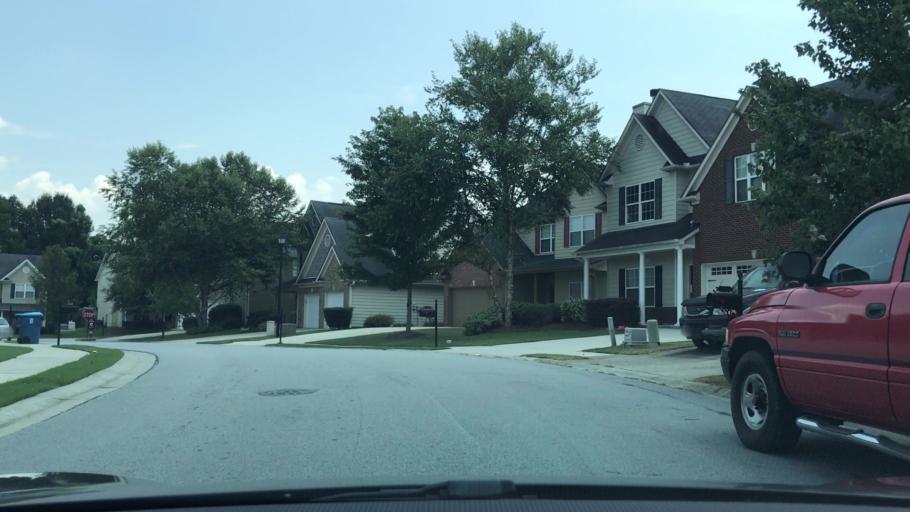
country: US
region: Georgia
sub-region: Jackson County
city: Braselton
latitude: 34.1223
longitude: -83.8240
